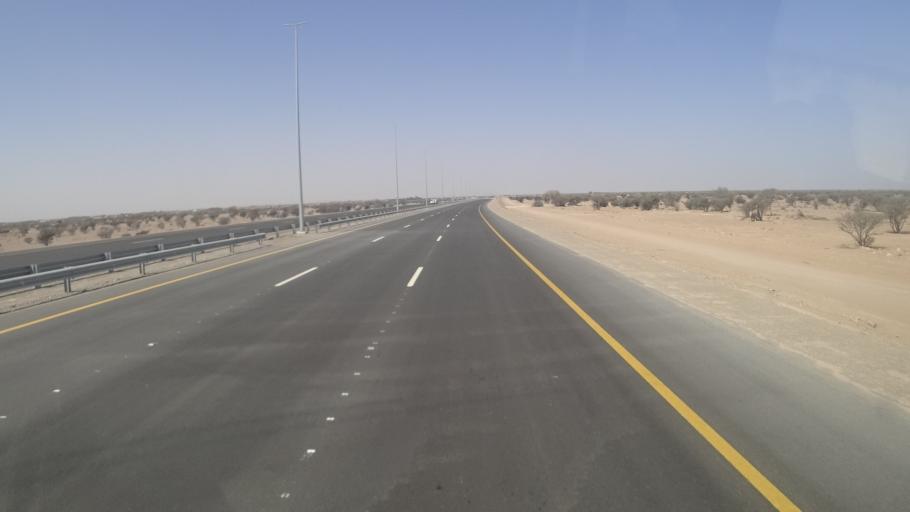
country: OM
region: Ash Sharqiyah
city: Sur
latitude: 22.2719
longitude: 59.2431
